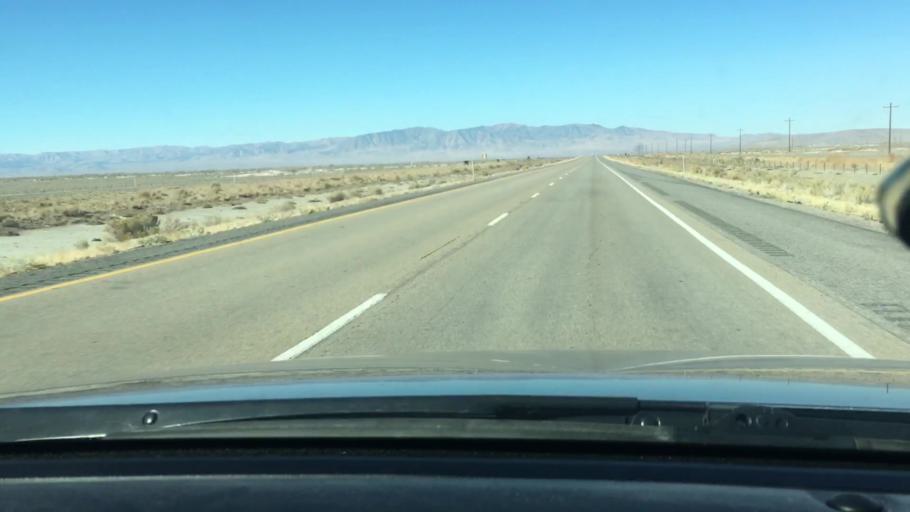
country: US
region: Utah
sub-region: Tooele County
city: Grantsville
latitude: 40.7483
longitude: -112.6758
